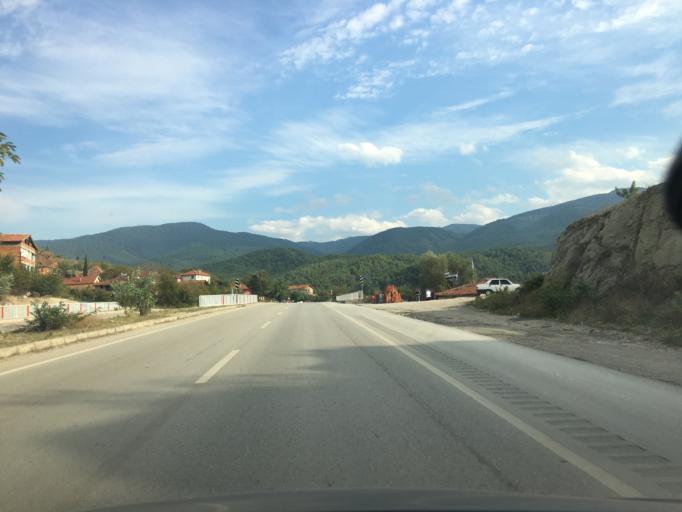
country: TR
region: Karabuk
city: Karabuk
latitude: 41.0968
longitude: 32.6755
